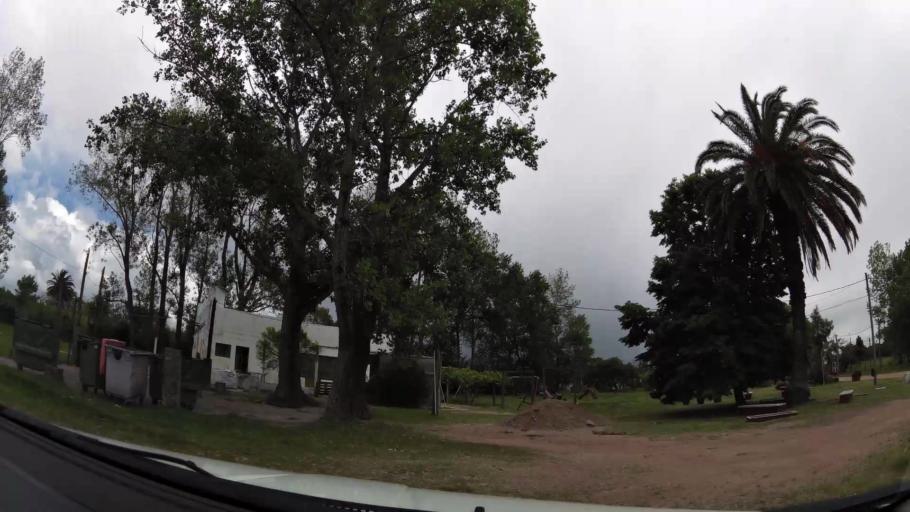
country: UY
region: Canelones
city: La Paz
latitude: -34.8033
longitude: -56.1571
